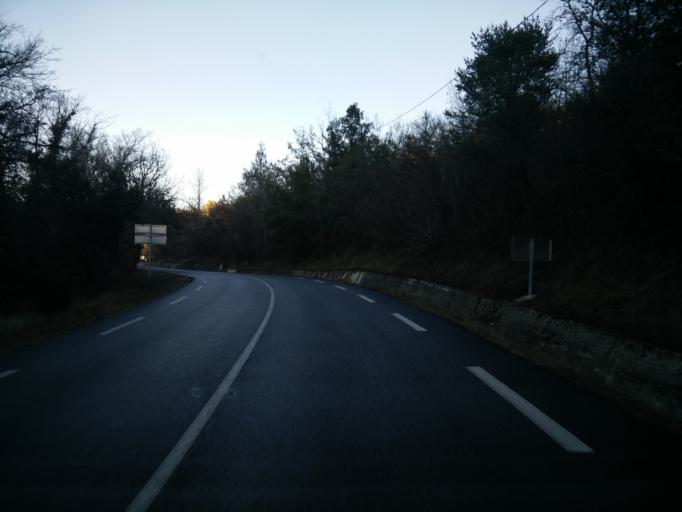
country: FR
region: Provence-Alpes-Cote d'Azur
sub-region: Departement du Var
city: Montferrat
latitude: 43.5970
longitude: 6.4716
